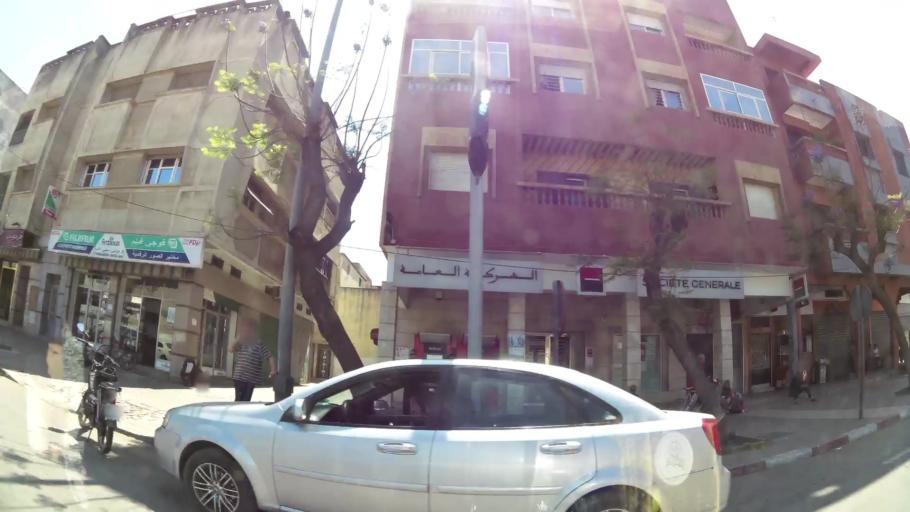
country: MA
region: Gharb-Chrarda-Beni Hssen
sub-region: Kenitra Province
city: Kenitra
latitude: 34.2459
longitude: -6.5527
